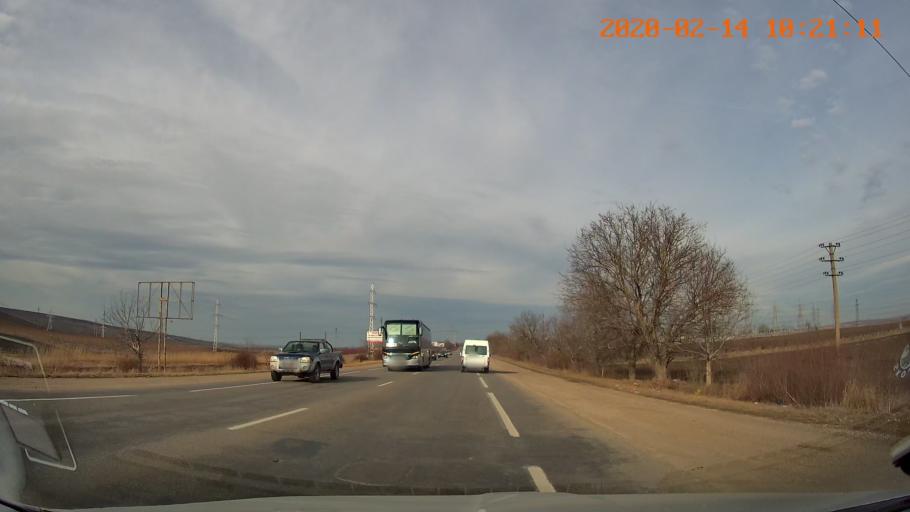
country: MD
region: Balti
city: Balti
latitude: 47.7955
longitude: 27.8734
